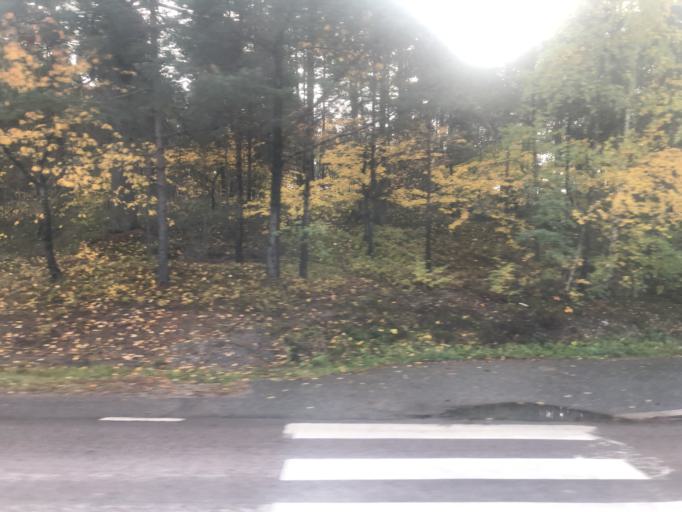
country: SE
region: Stockholm
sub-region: Jarfalla Kommun
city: Jakobsberg
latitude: 59.4061
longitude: 17.8451
